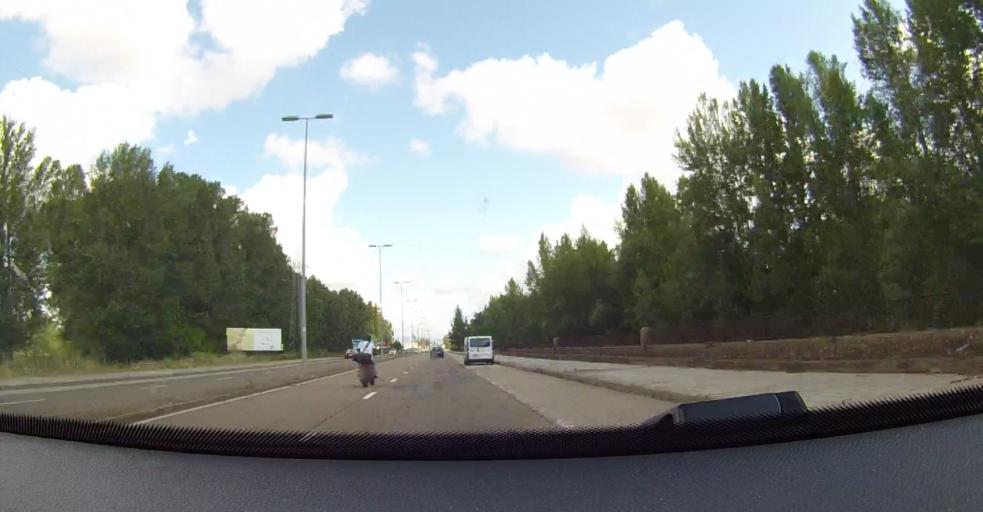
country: ES
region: Castille and Leon
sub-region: Provincia de Leon
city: Leon
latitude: 42.5745
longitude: -5.5687
